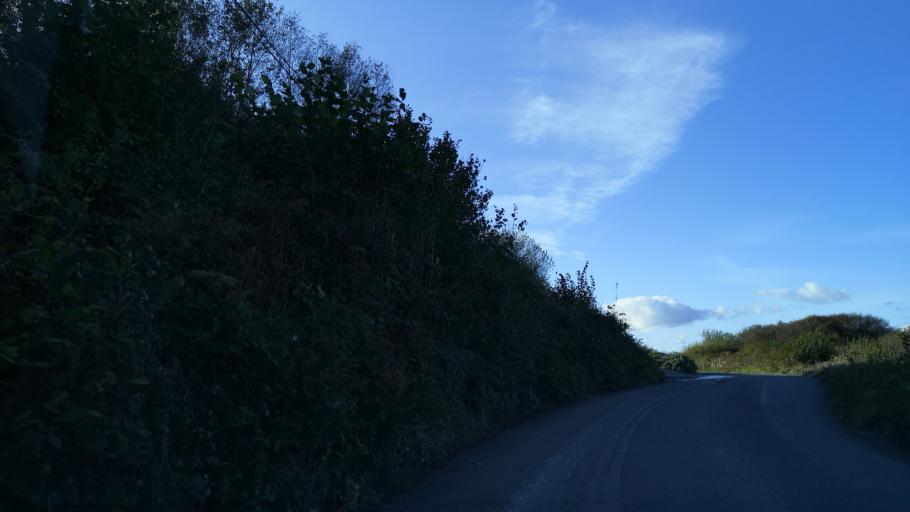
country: IE
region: Connaught
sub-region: County Galway
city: Clifden
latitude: 53.5055
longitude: -10.0426
